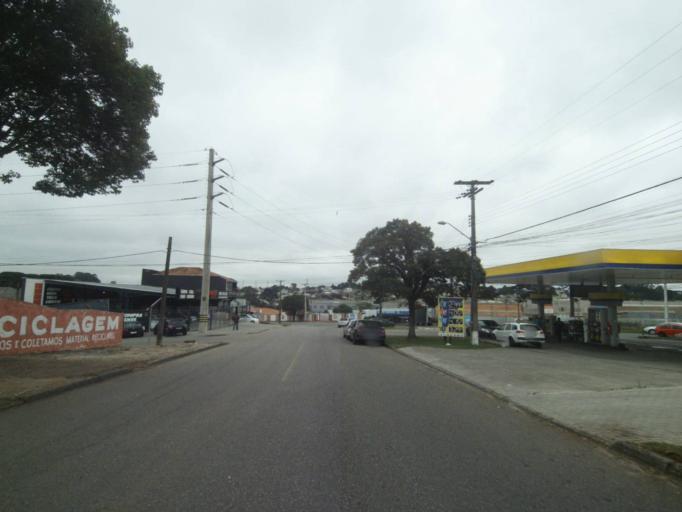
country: BR
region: Parana
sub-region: Sao Jose Dos Pinhais
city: Sao Jose dos Pinhais
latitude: -25.5371
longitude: -49.2823
